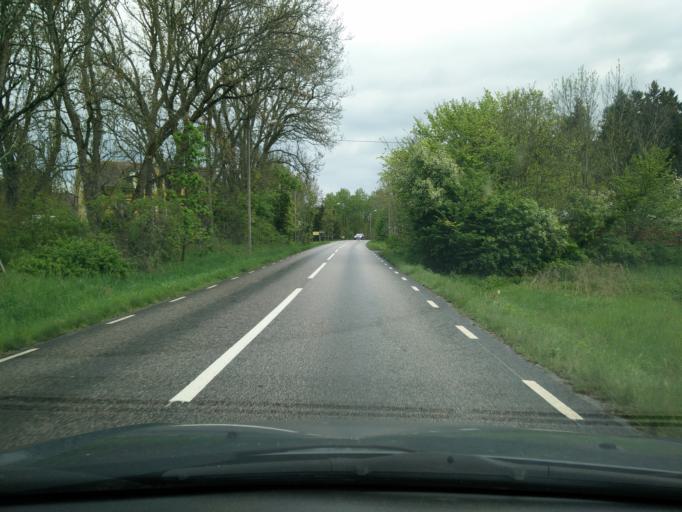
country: SE
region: Stockholm
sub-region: Norrtalje Kommun
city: Bjorko
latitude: 59.8171
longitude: 18.8938
